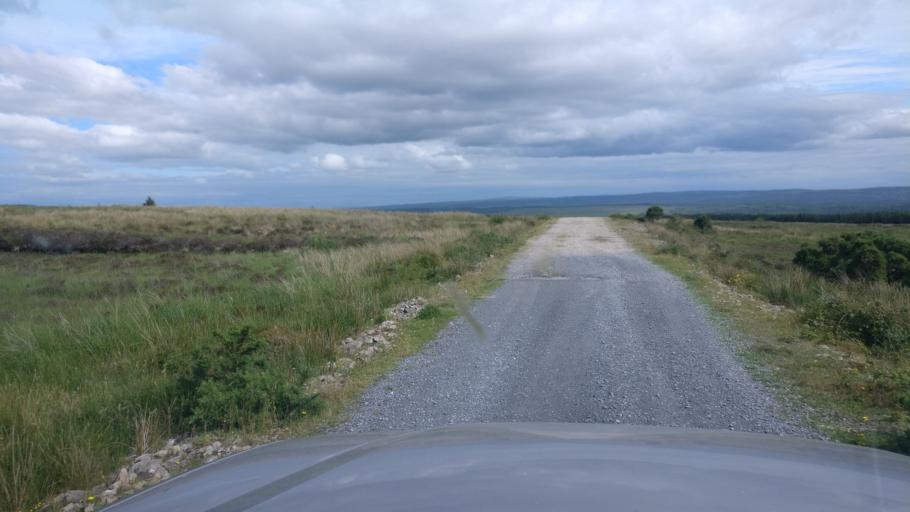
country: IE
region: Connaught
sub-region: County Galway
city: Gort
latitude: 53.0776
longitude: -8.6815
